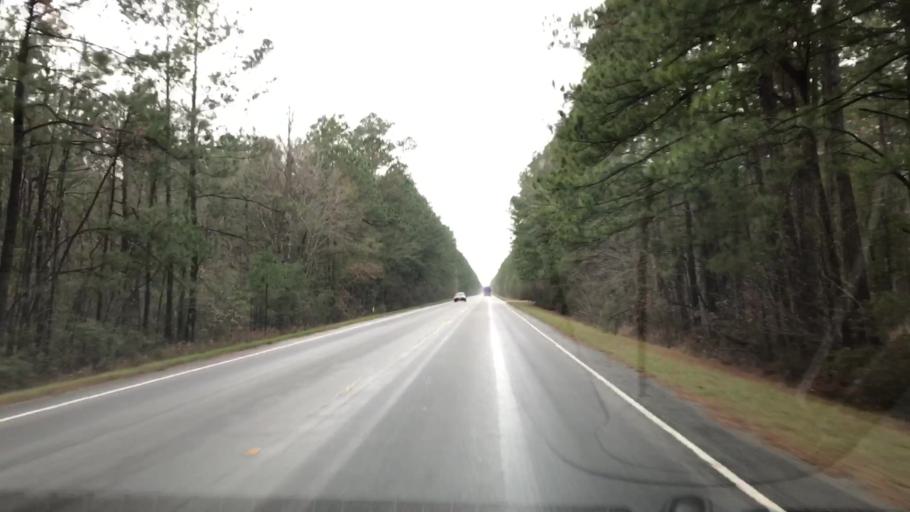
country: US
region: South Carolina
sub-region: Berkeley County
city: Saint Stephen
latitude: 33.2873
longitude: -79.8415
